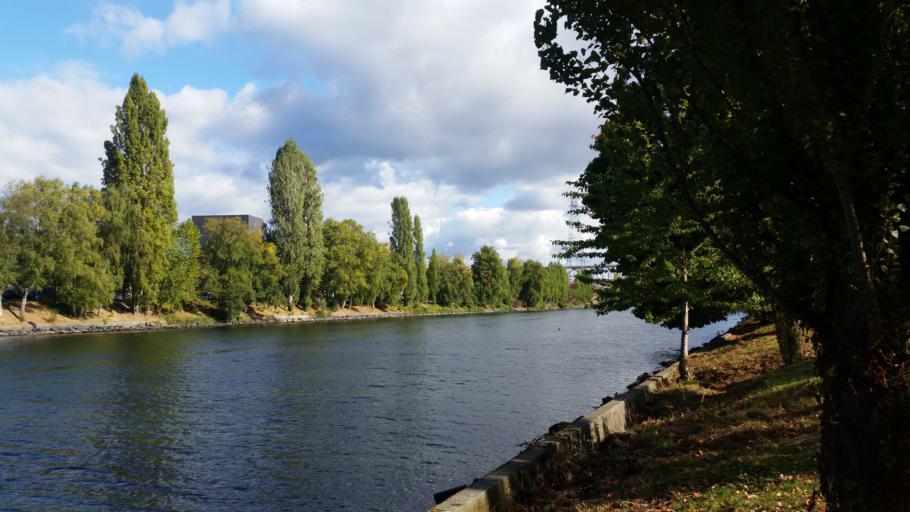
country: US
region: Washington
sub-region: King County
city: Seattle
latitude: 47.6513
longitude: -122.3589
